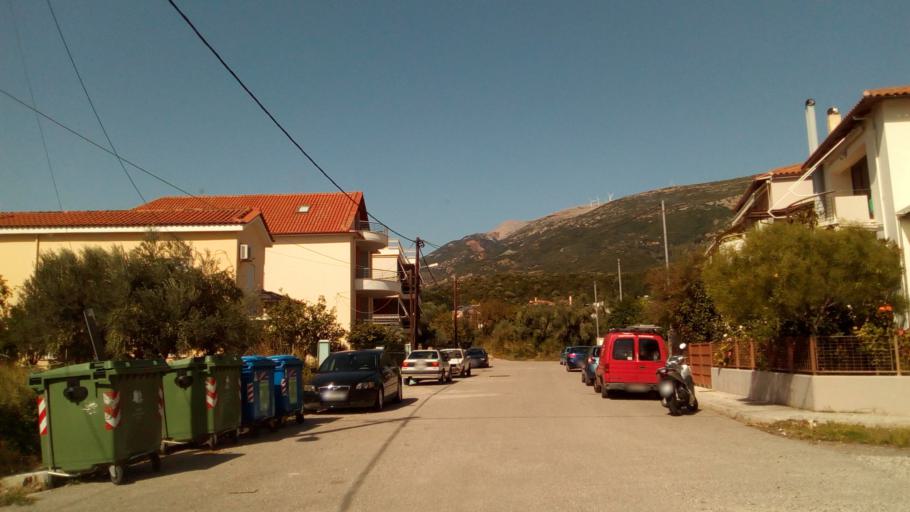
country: GR
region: West Greece
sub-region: Nomos Aitolias kai Akarnanias
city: Nafpaktos
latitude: 38.3907
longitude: 21.8155
